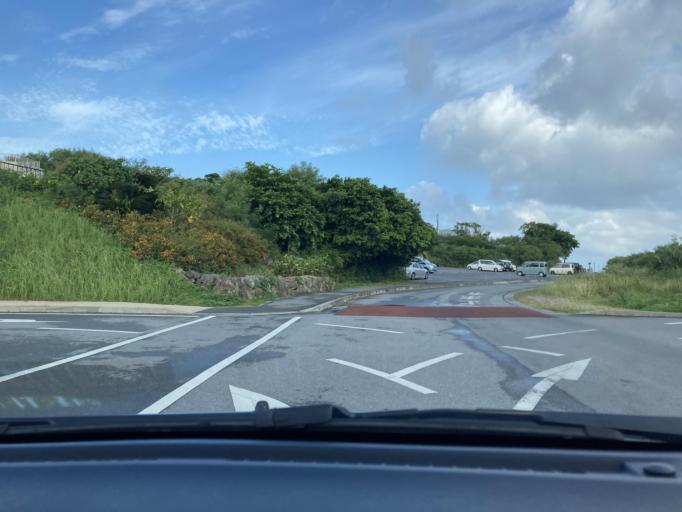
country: JP
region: Okinawa
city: Tomigusuku
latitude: 26.1746
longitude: 127.6433
